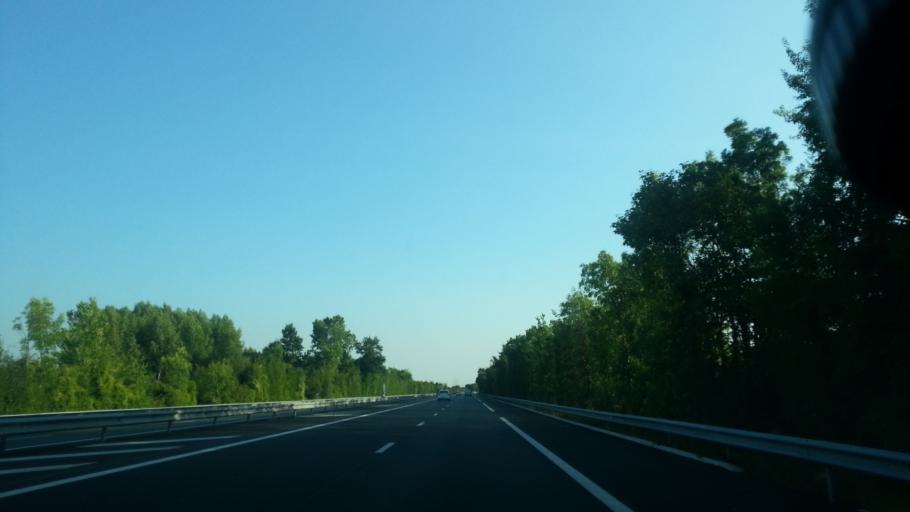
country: FR
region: Poitou-Charentes
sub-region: Departement des Deux-Sevres
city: Beauvoir-sur-Niort
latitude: 46.1270
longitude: -0.5309
